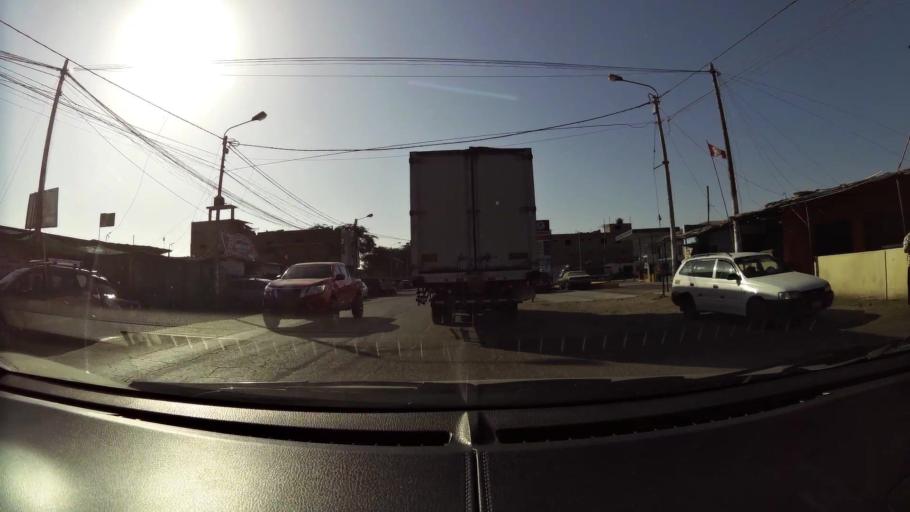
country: PE
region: Ancash
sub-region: Provincia de Casma
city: Casma
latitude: -9.4773
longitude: -78.2945
